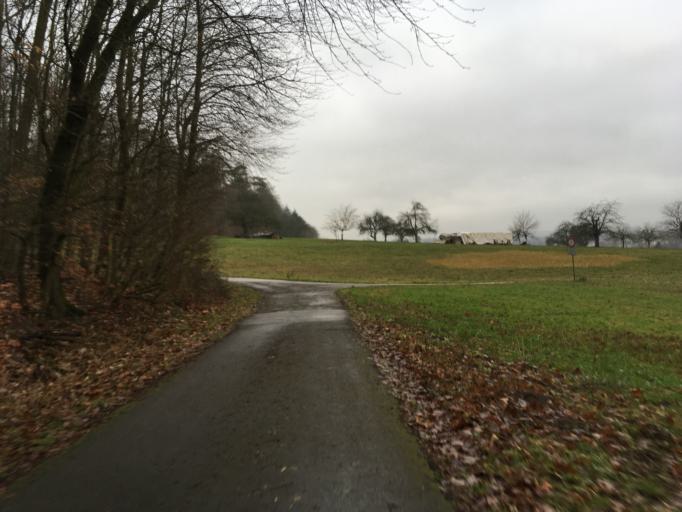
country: DE
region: Baden-Wuerttemberg
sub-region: Karlsruhe Region
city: Konigsbach-Stein
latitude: 48.9552
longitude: 8.5259
